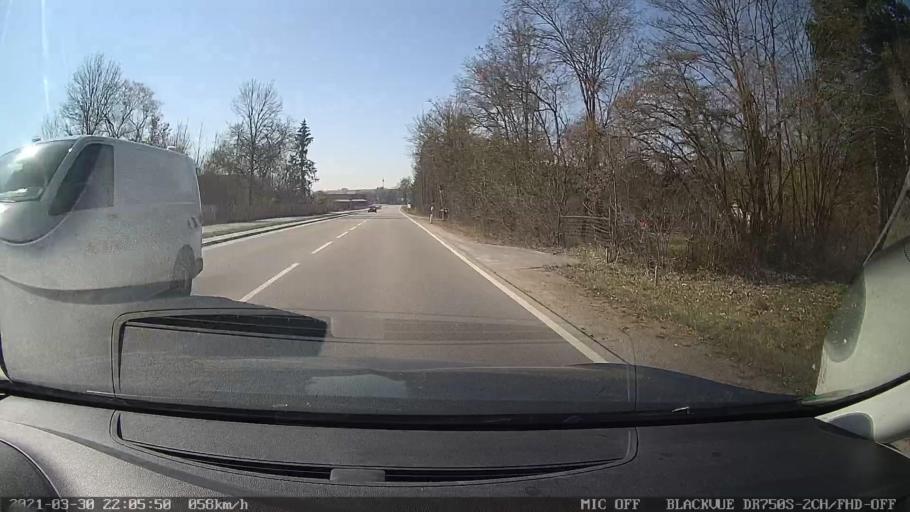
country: DE
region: Bavaria
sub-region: Upper Palatinate
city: Zeitlarn
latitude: 49.0948
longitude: 12.1223
